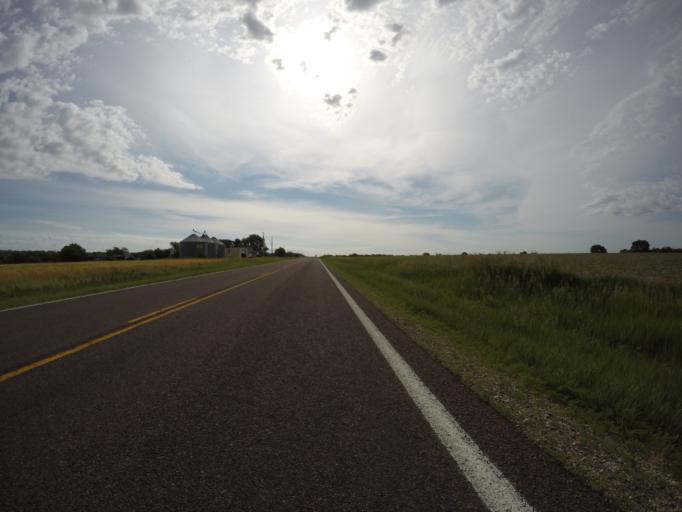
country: US
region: Kansas
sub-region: Washington County
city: Washington
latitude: 39.7120
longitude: -97.3179
